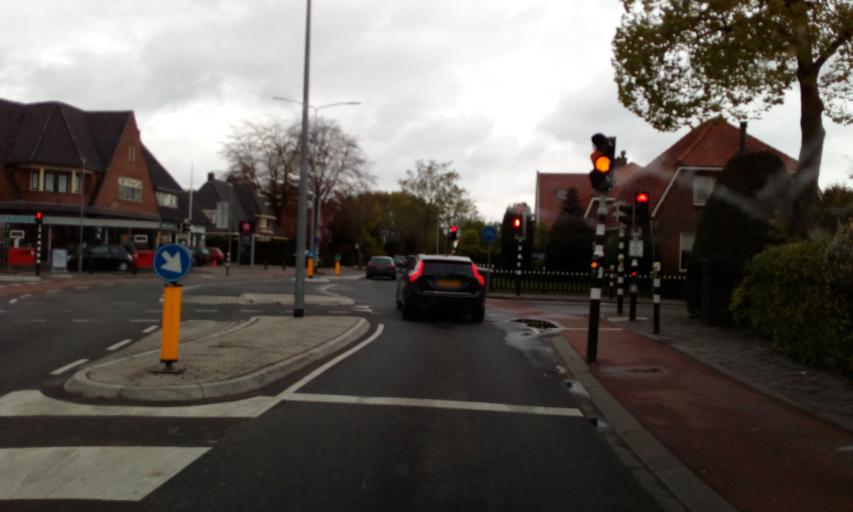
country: NL
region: North Holland
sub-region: Gemeente Huizen
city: Huizen
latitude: 52.2946
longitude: 5.2348
